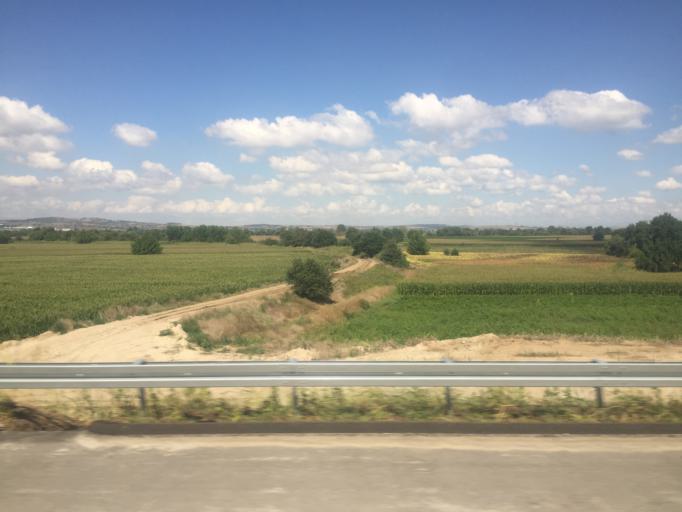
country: TR
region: Balikesir
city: Gobel
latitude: 40.0243
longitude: 28.2078
